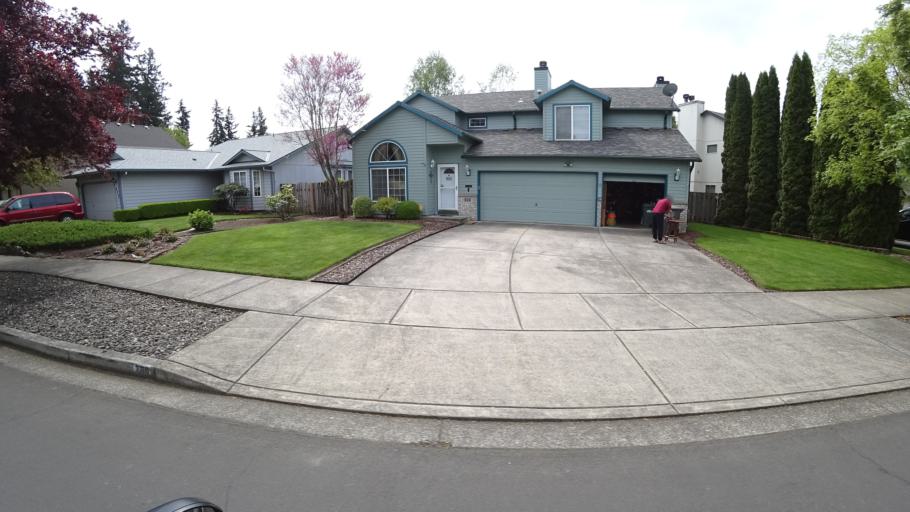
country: US
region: Oregon
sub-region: Washington County
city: Hillsboro
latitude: 45.5457
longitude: -122.9912
